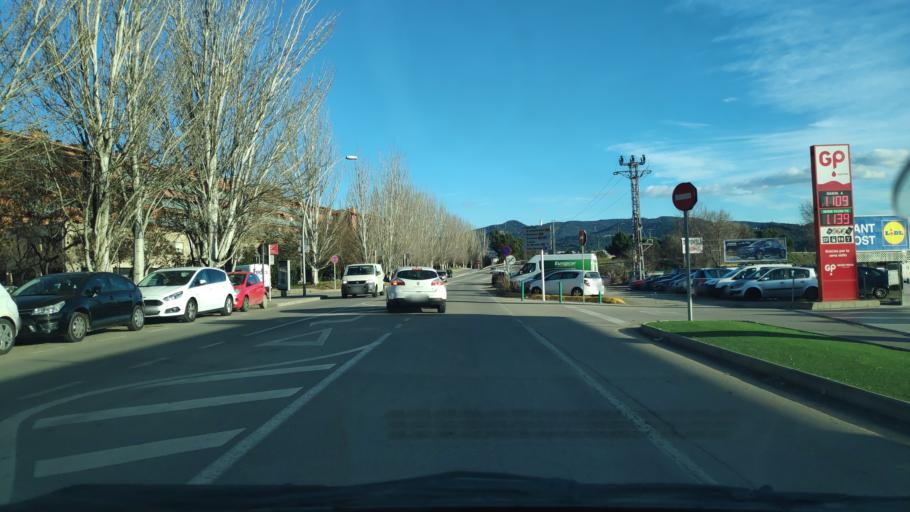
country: ES
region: Catalonia
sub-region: Provincia de Barcelona
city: Mollet del Valles
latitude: 41.5337
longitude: 2.2126
